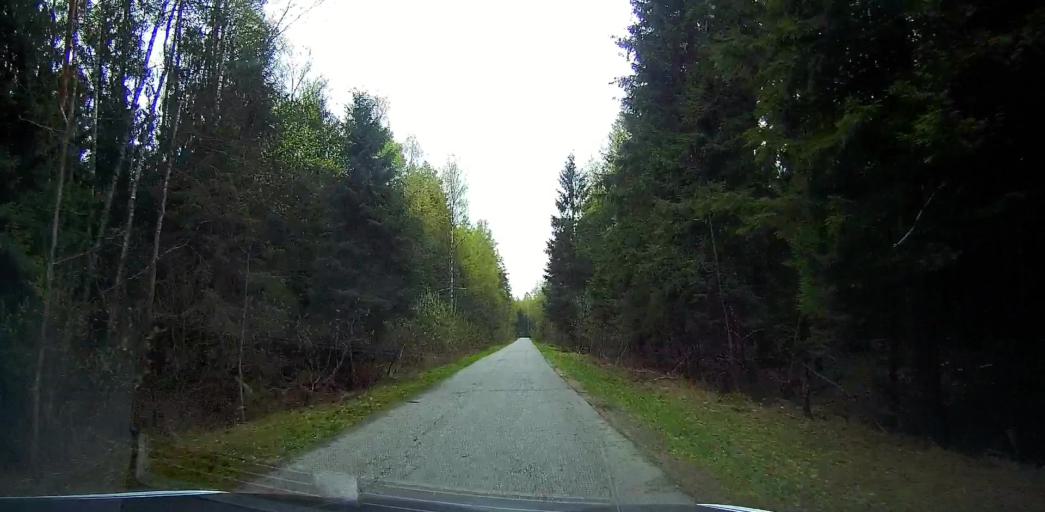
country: RU
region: Moskovskaya
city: Malyshevo
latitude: 55.5398
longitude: 38.3849
